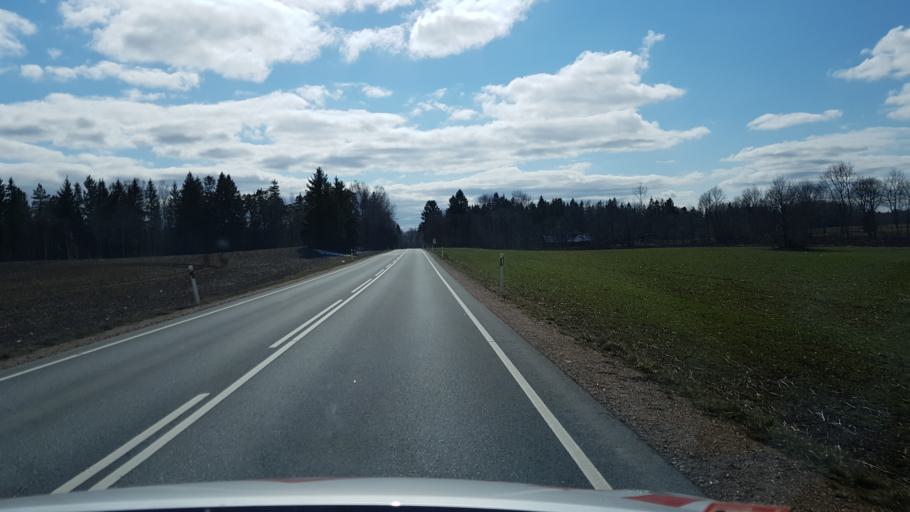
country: EE
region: Laeaene-Virumaa
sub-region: Tapa vald
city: Tapa
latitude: 59.3618
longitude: 26.0005
